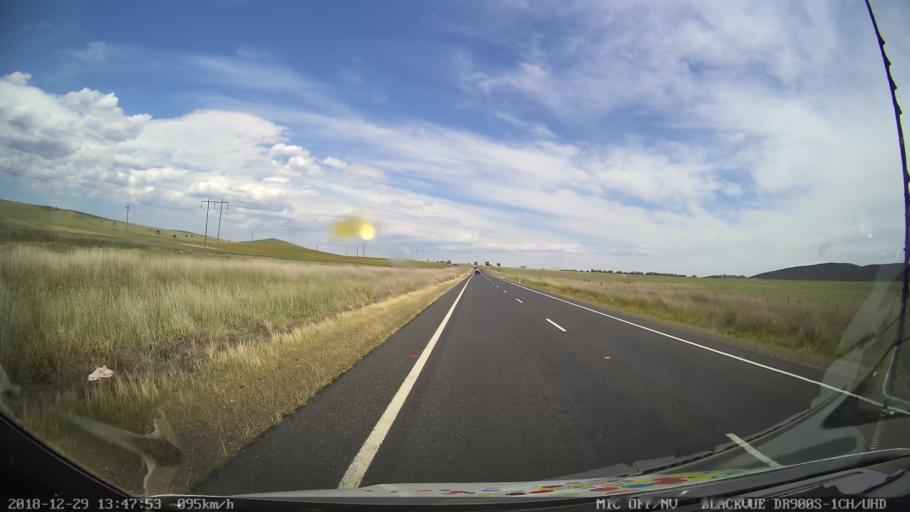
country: AU
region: New South Wales
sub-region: Cooma-Monaro
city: Cooma
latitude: -36.1328
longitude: 149.1452
